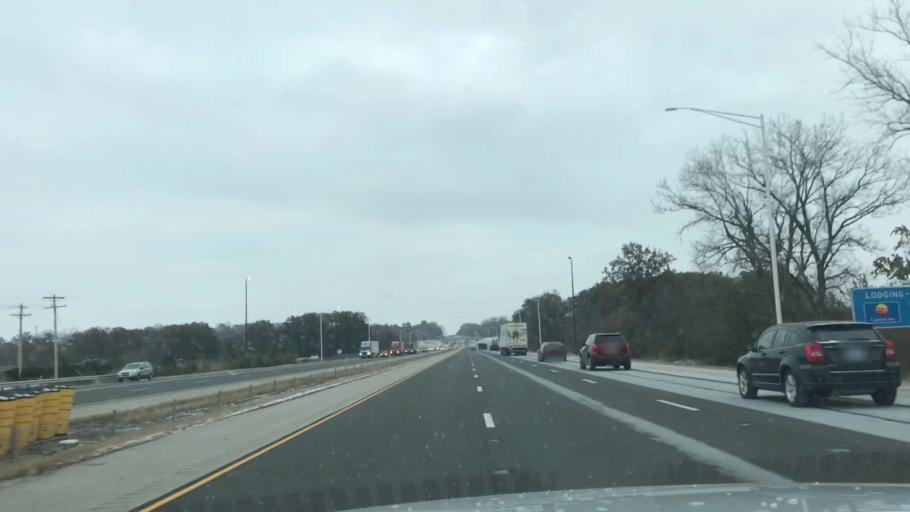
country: US
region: Illinois
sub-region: Madison County
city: Glen Carbon
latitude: 38.7567
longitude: -90.0225
